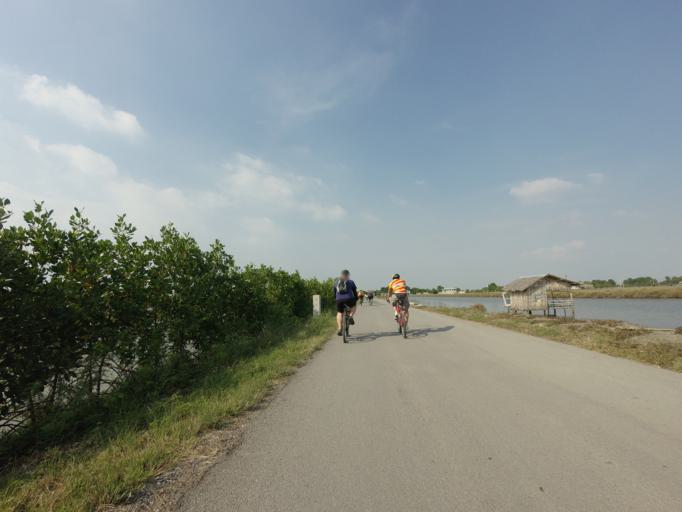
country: TH
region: Samut Sakhon
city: Samut Sakhon
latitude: 13.4959
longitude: 100.3615
